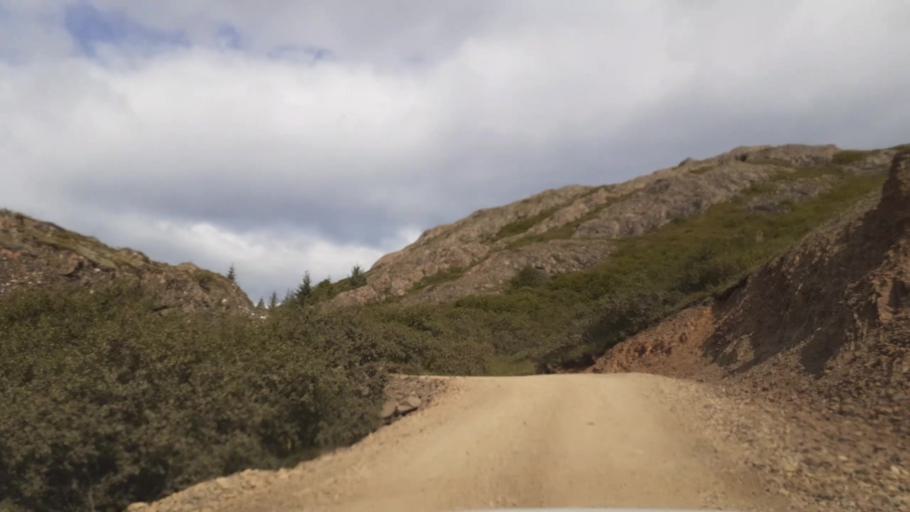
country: IS
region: East
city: Hoefn
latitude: 64.4382
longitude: -14.9124
